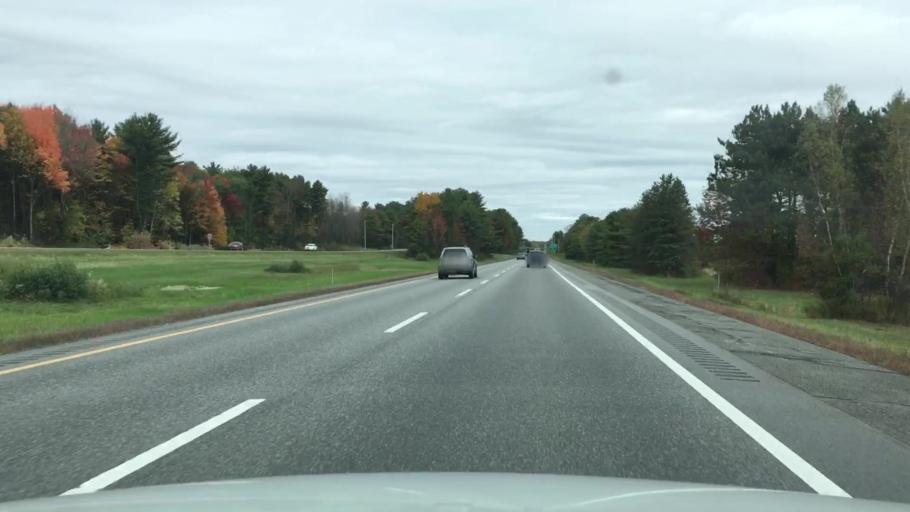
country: US
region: Maine
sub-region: Kennebec County
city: Oakland
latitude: 44.4989
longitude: -69.7040
